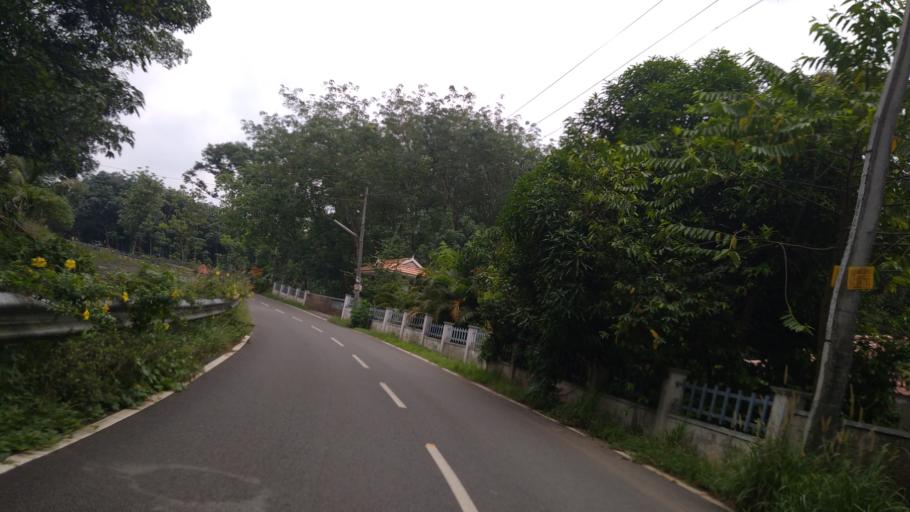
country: IN
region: Kerala
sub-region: Ernakulam
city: Ramamangalam
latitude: 10.0180
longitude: 76.4868
